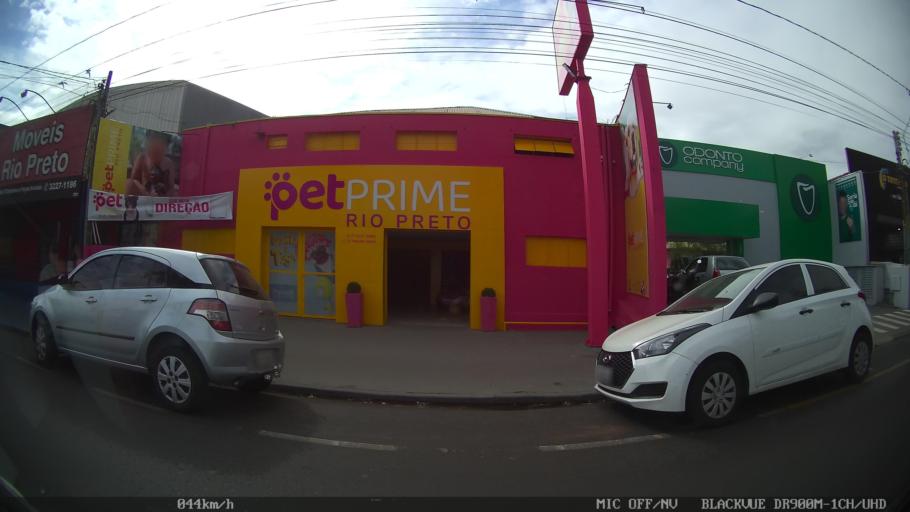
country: BR
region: Sao Paulo
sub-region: Sao Jose Do Rio Preto
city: Sao Jose do Rio Preto
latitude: -20.8262
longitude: -49.3735
